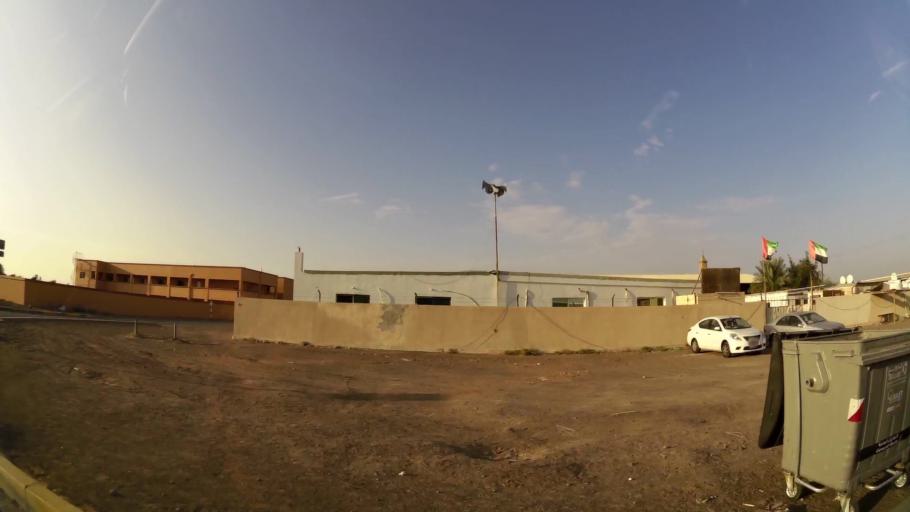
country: AE
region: Abu Dhabi
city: Al Ain
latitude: 24.1460
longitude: 55.8315
